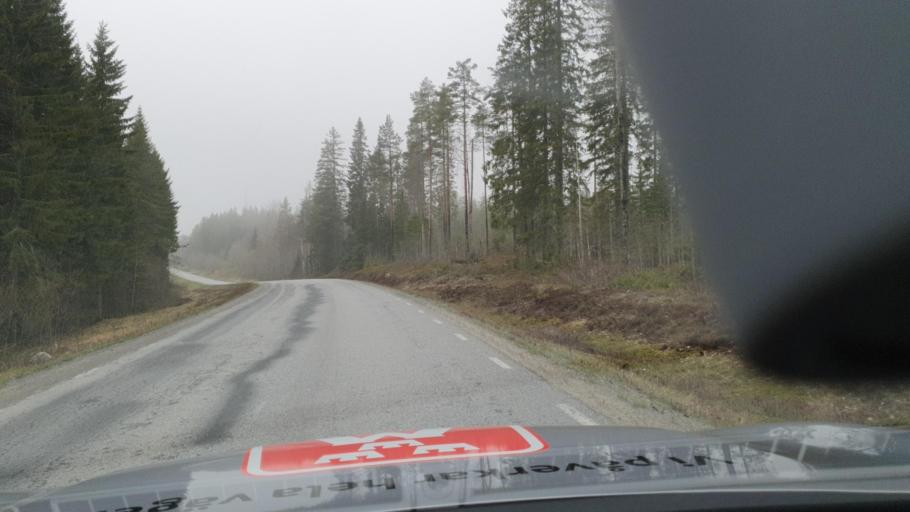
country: SE
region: Vaesternorrland
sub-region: OErnskoeldsviks Kommun
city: Husum
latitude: 63.4836
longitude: 19.2037
